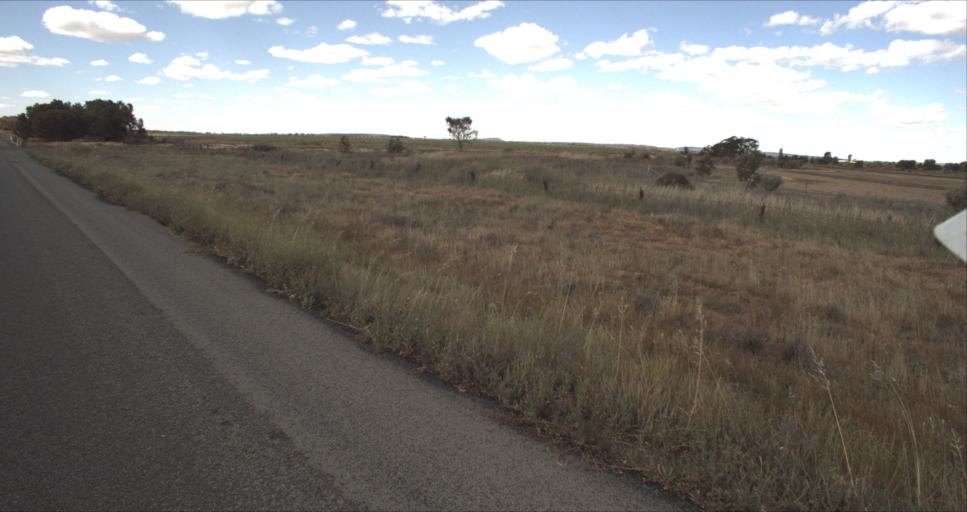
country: AU
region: New South Wales
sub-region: Leeton
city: Leeton
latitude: -34.4420
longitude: 146.2562
